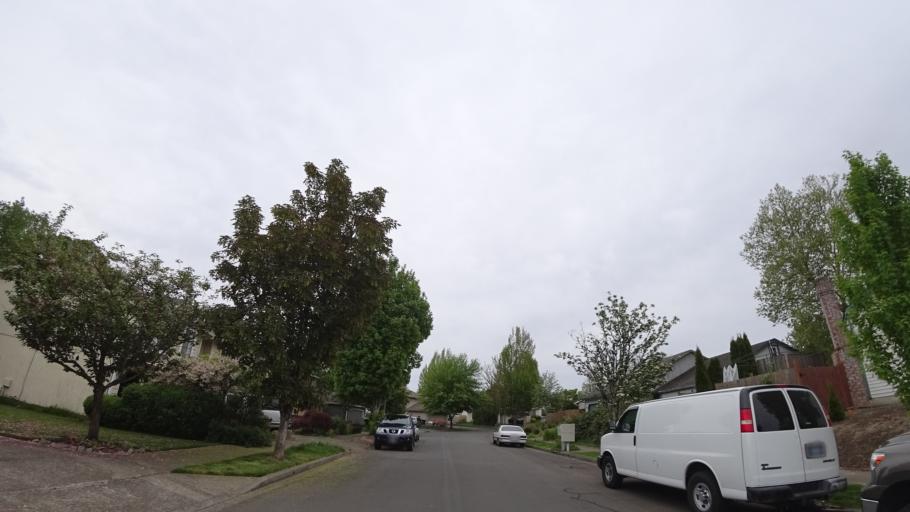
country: US
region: Oregon
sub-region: Washington County
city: Aloha
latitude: 45.5063
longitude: -122.9064
